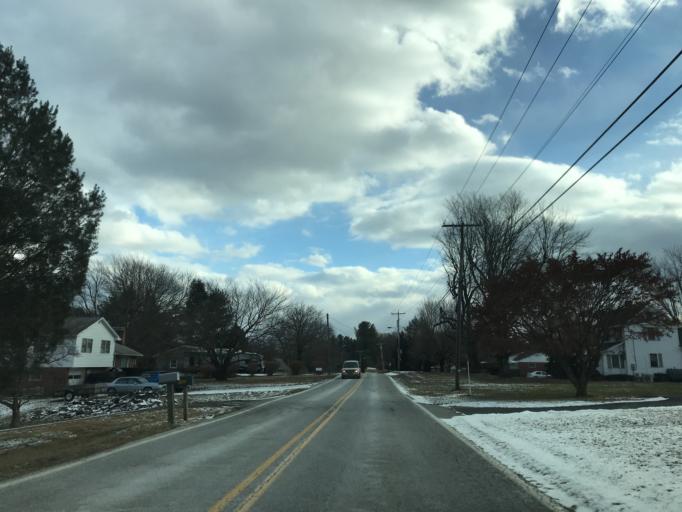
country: US
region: Maryland
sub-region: Harford County
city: Jarrettsville
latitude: 39.6180
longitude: -76.4515
